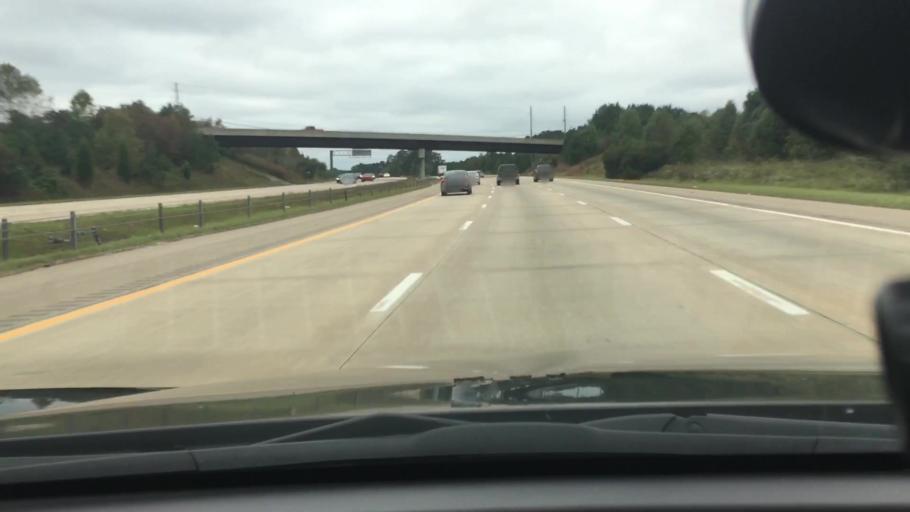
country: US
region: North Carolina
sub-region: Wake County
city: Knightdale
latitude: 35.7670
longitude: -78.4853
